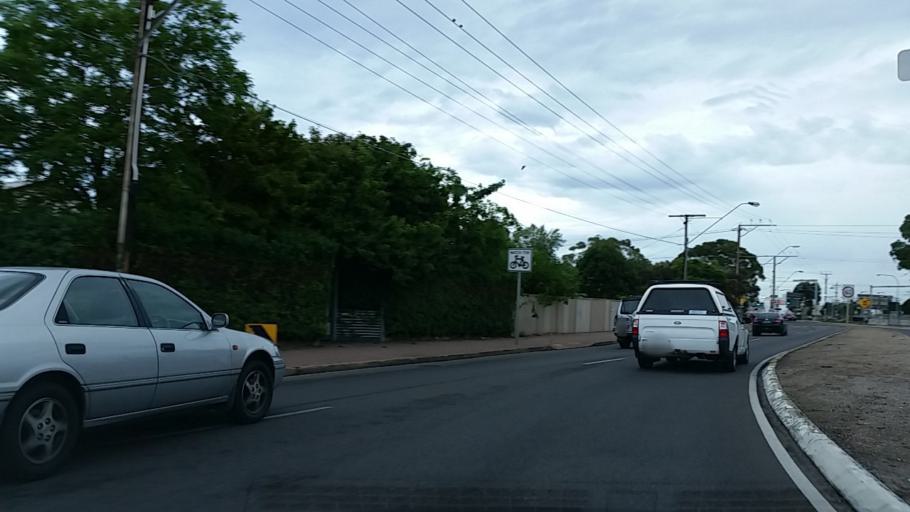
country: AU
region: South Australia
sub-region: Marion
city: Sturt
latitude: -35.0118
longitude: 138.5405
